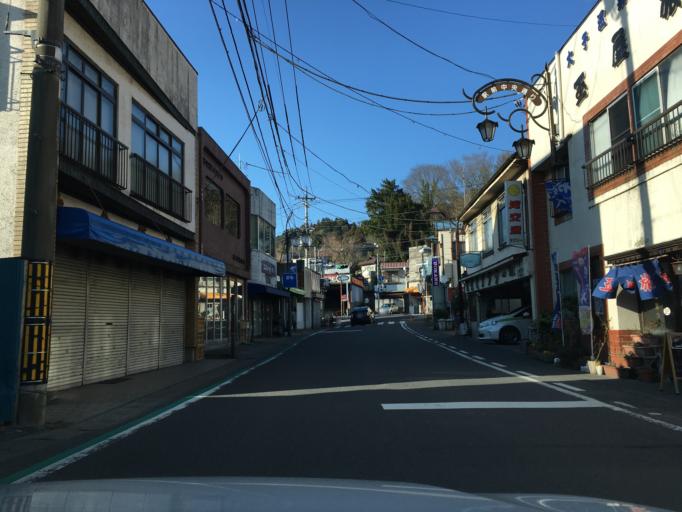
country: JP
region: Ibaraki
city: Daigo
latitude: 36.7713
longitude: 140.3513
